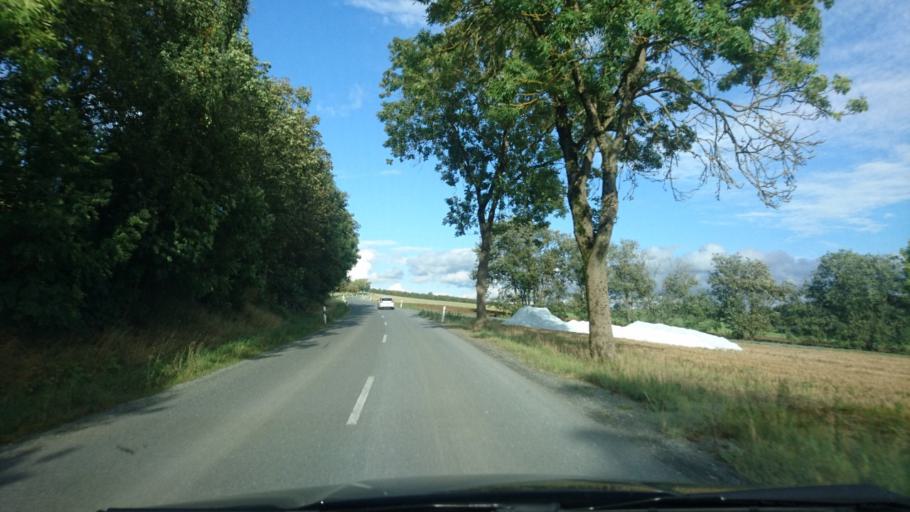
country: DE
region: Bavaria
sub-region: Upper Franconia
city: Berg
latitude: 50.3652
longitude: 11.7650
